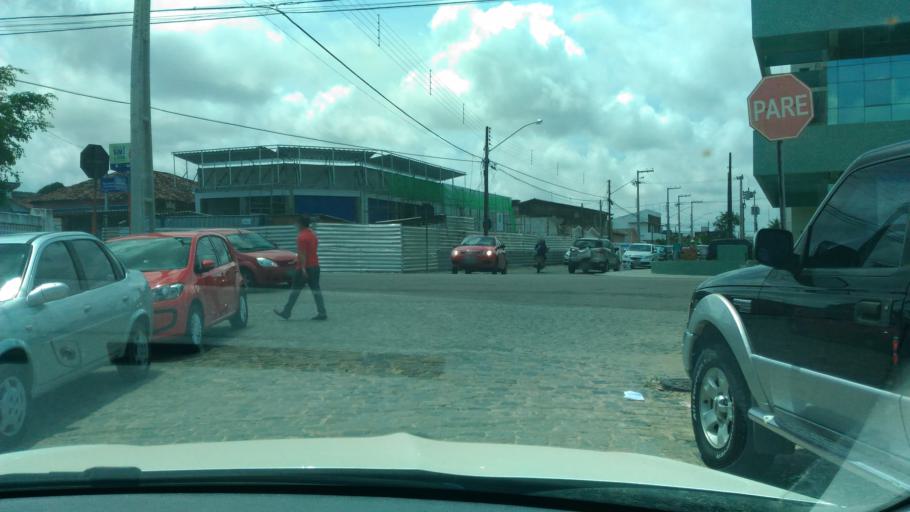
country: BR
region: Paraiba
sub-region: Joao Pessoa
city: Joao Pessoa
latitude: -7.1230
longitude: -34.8587
